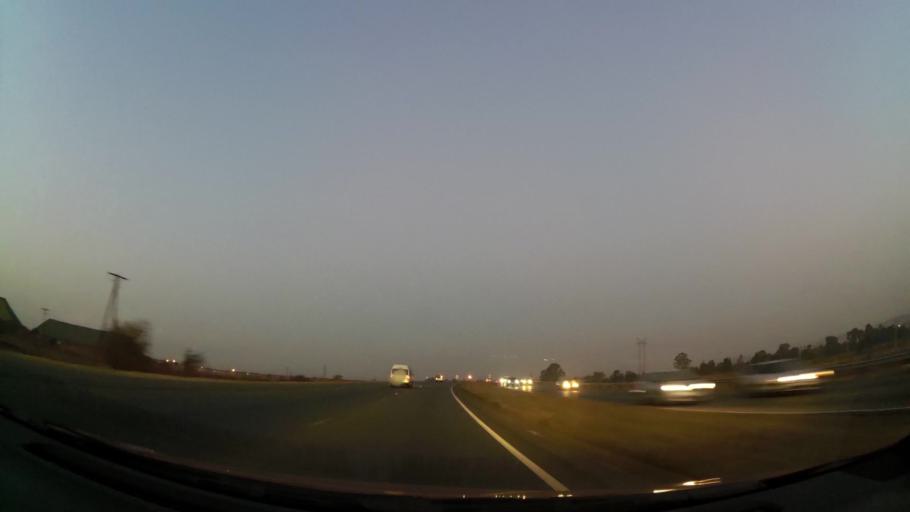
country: ZA
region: Gauteng
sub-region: City of Johannesburg Metropolitan Municipality
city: Soweto
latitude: -26.2947
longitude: 27.8400
